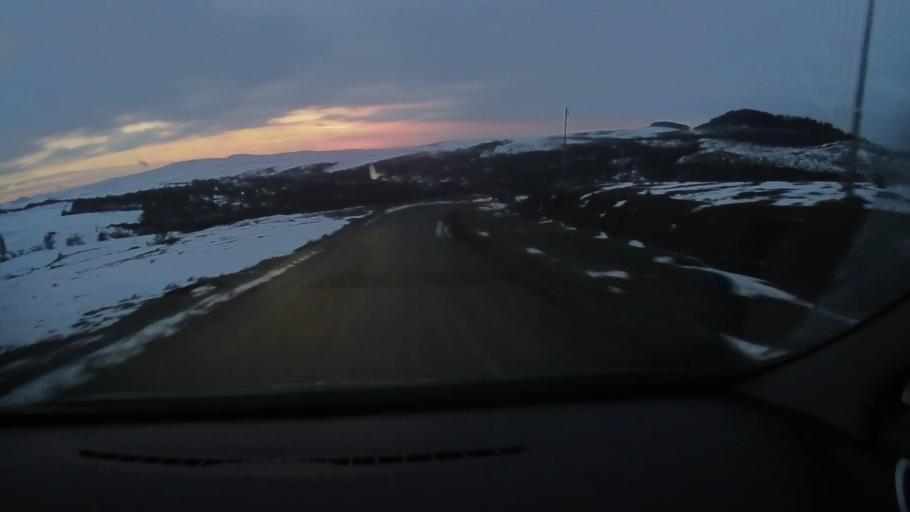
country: RO
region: Harghita
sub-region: Comuna Darjiu
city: Darjiu
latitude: 46.1759
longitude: 25.2471
